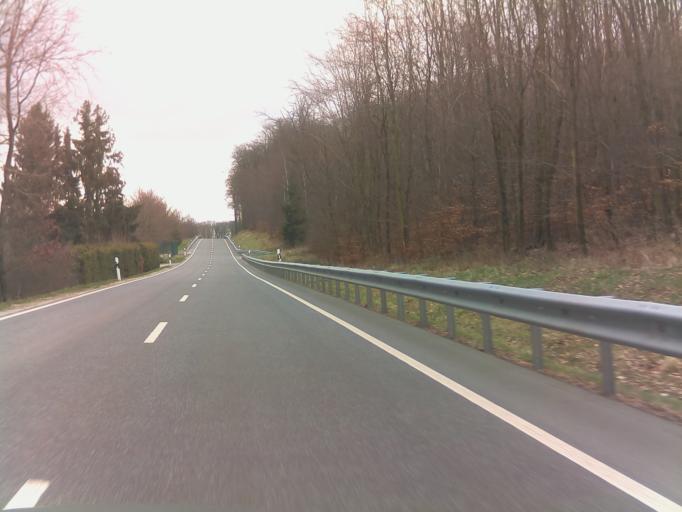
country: DE
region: Rheinland-Pfalz
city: Dorrebach
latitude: 49.9551
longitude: 7.6787
